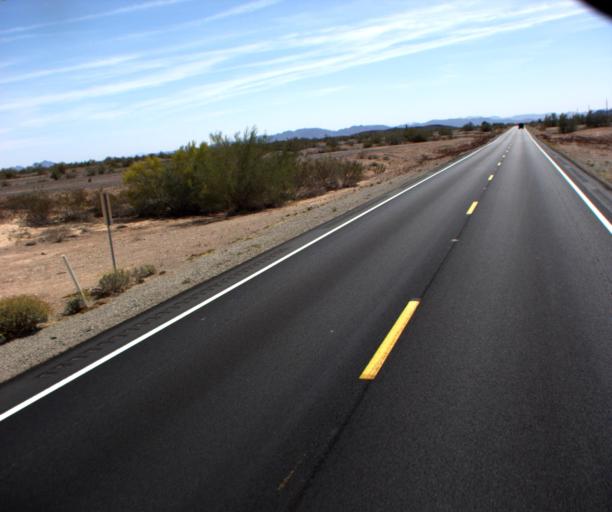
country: US
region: Arizona
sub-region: Yuma County
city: Wellton
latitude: 32.9850
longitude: -114.2885
